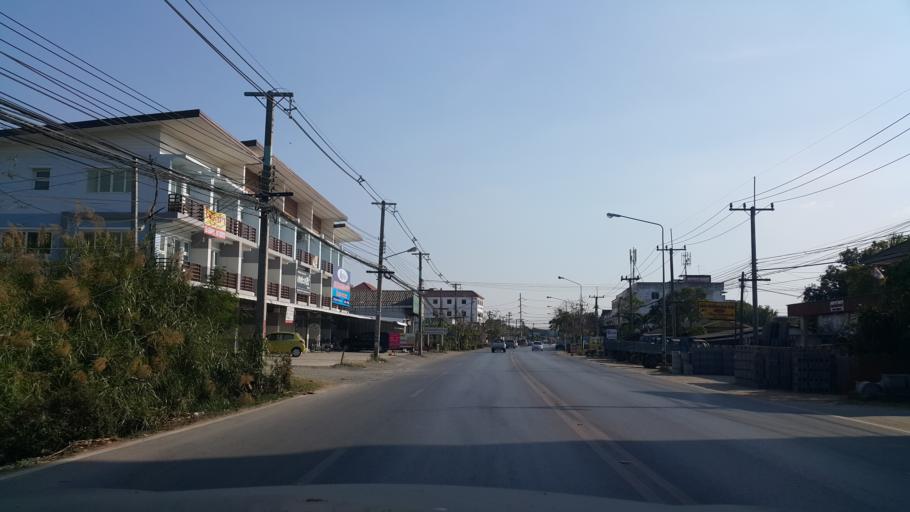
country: TH
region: Chiang Mai
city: San Sai
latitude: 18.8354
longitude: 99.0423
